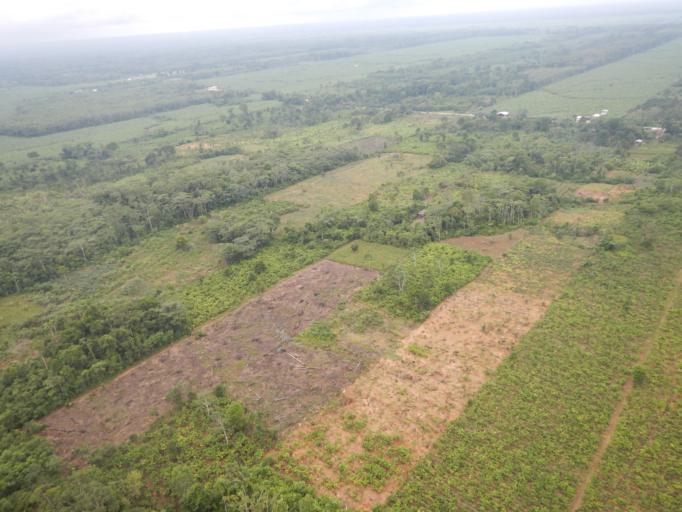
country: BO
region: Cochabamba
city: Chimore
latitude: -17.1890
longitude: -64.7450
